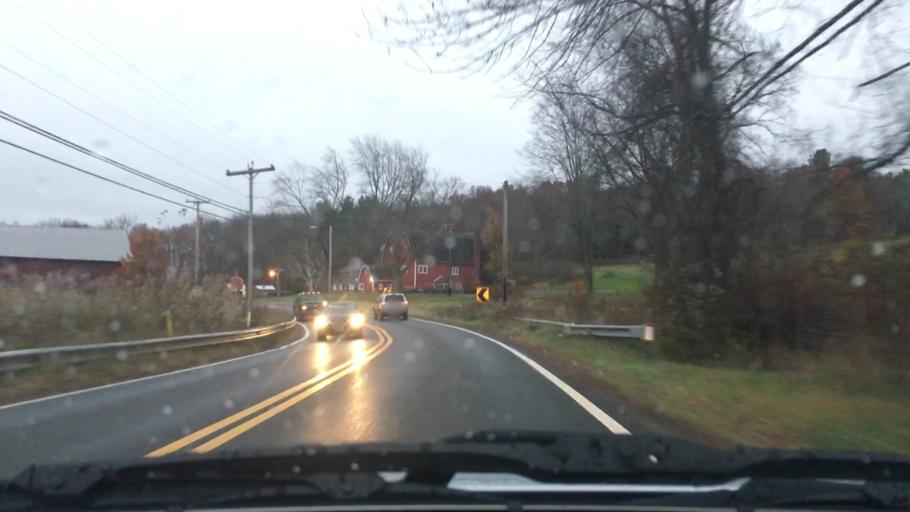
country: US
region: Massachusetts
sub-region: Hampden County
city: Southwick
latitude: 42.0760
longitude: -72.7688
